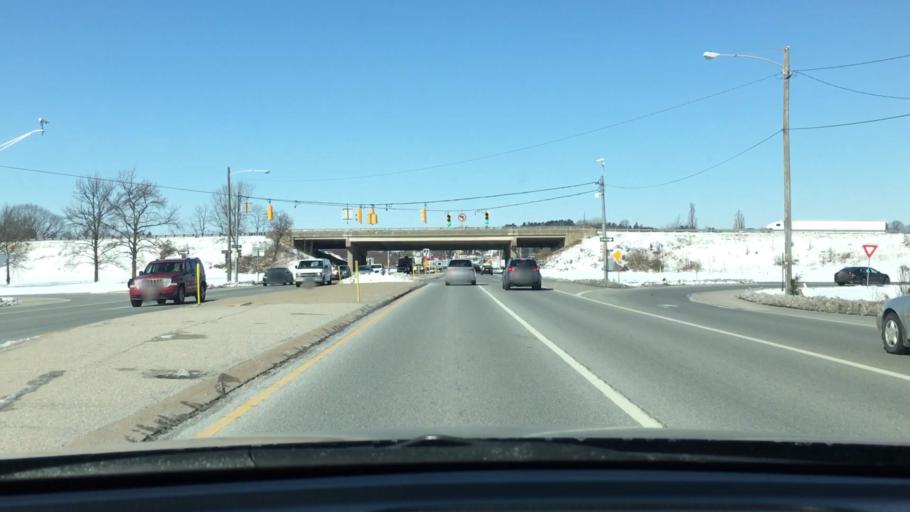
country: US
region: Pennsylvania
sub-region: York County
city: West York
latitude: 39.9646
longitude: -76.7696
